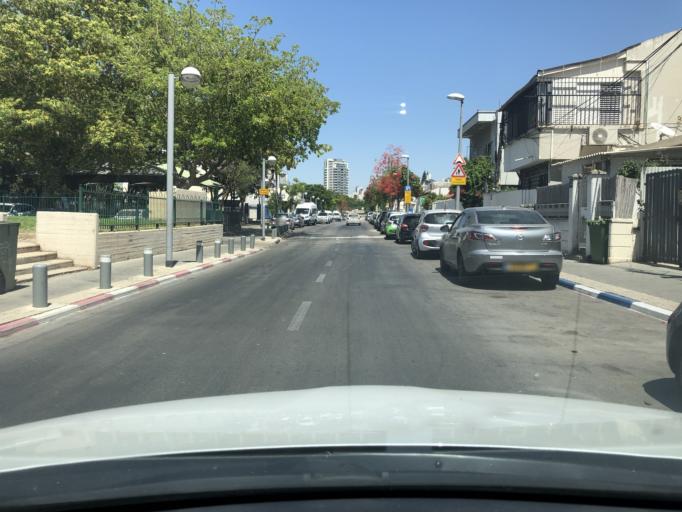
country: IL
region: Tel Aviv
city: Azor
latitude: 32.0466
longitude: 34.7923
